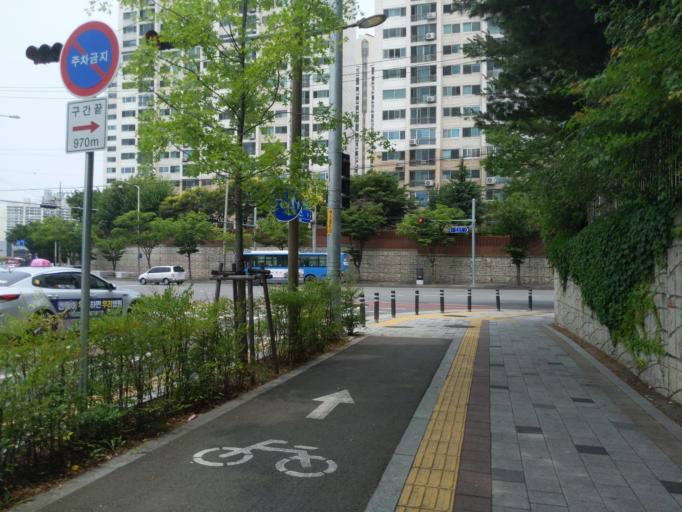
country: KR
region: Daegu
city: Hwawon
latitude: 35.8072
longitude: 128.5284
